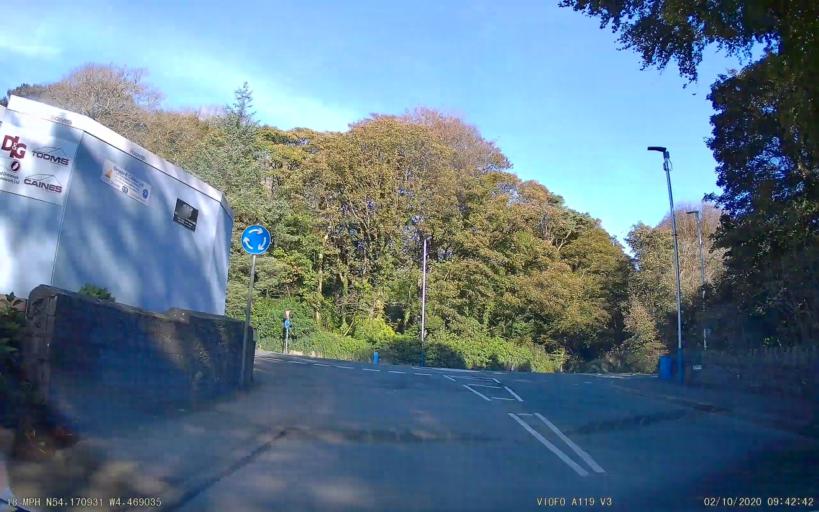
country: IM
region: Douglas
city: Douglas
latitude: 54.1710
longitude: -4.4691
